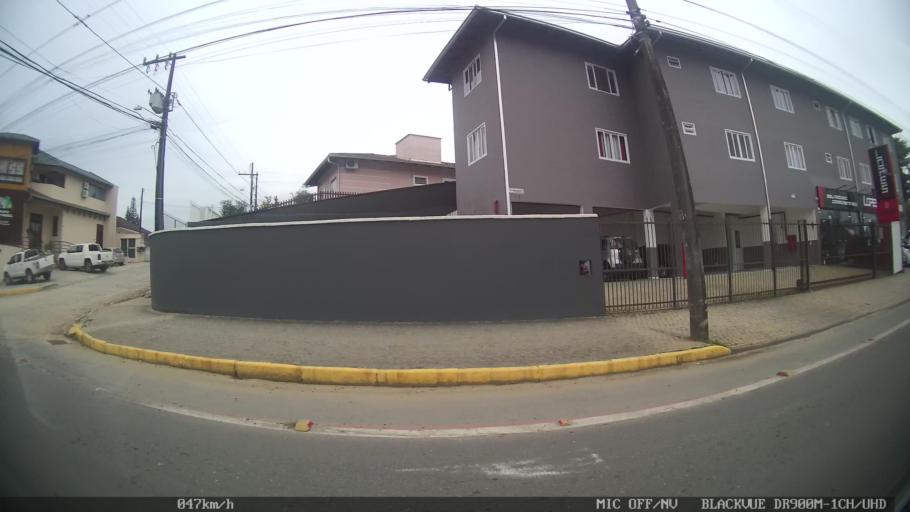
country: BR
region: Santa Catarina
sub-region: Joinville
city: Joinville
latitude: -26.2755
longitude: -48.8312
